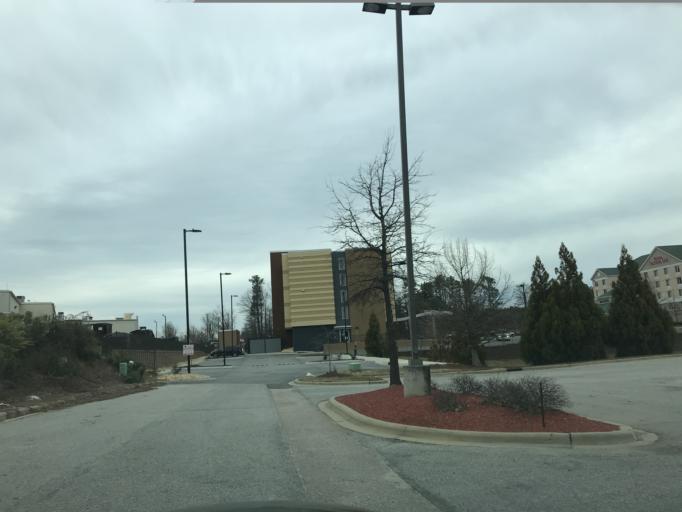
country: US
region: North Carolina
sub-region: Wake County
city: Raleigh
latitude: 35.8709
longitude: -78.5776
